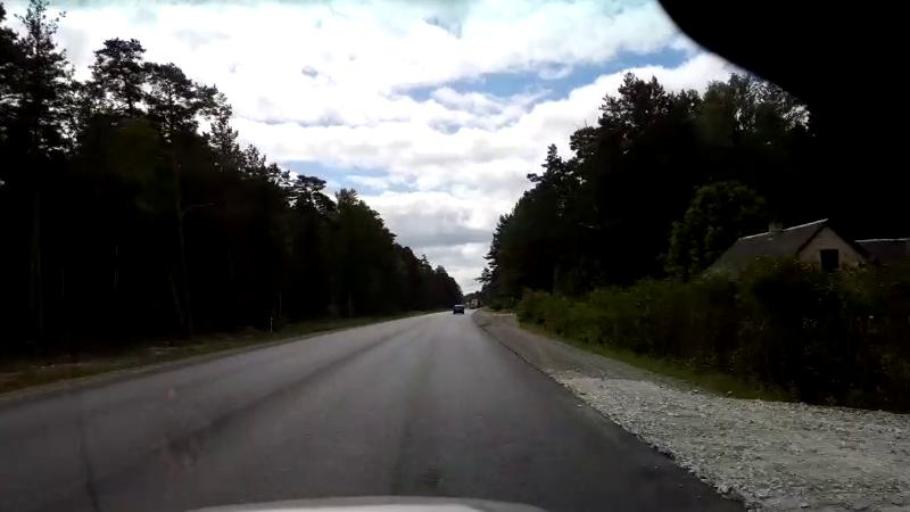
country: LV
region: Salacgrivas
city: Ainazi
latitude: 57.8159
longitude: 24.3472
